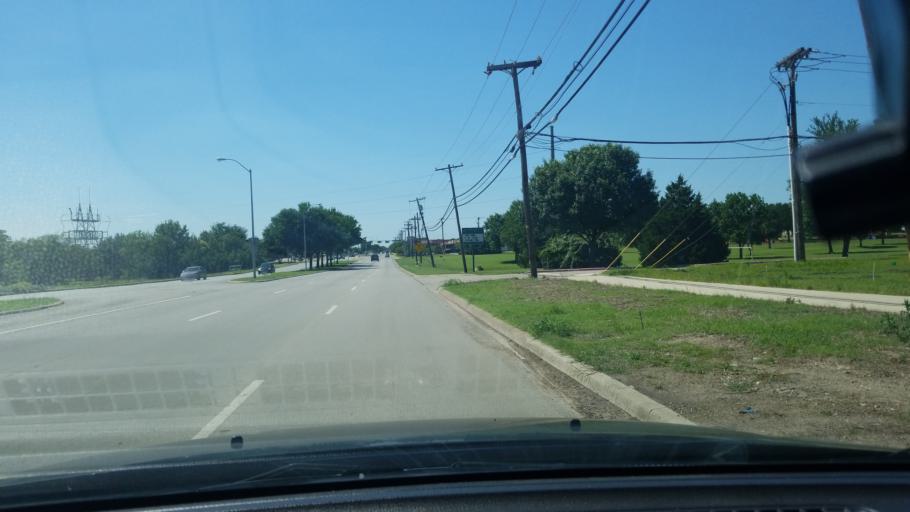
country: US
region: Texas
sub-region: Dallas County
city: Mesquite
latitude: 32.7747
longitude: -96.6165
